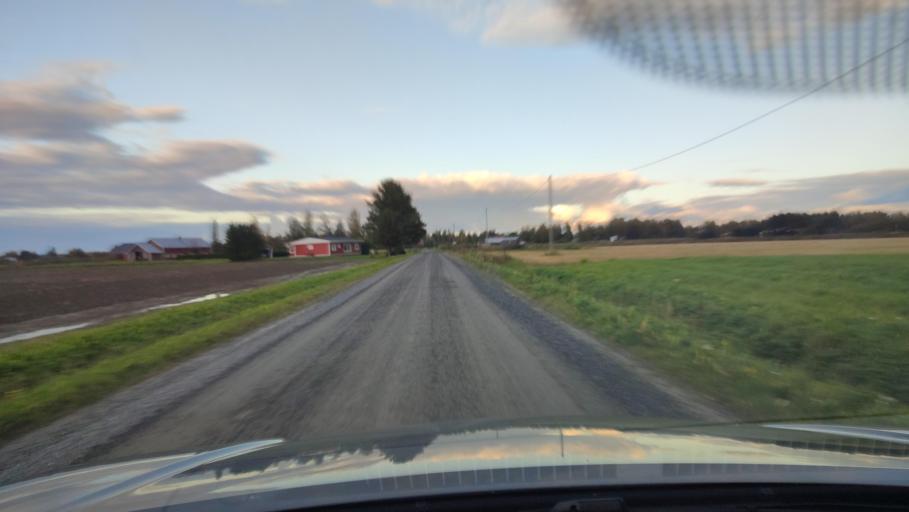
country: FI
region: Ostrobothnia
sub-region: Sydosterbotten
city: Kristinestad
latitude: 62.2512
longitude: 21.4851
